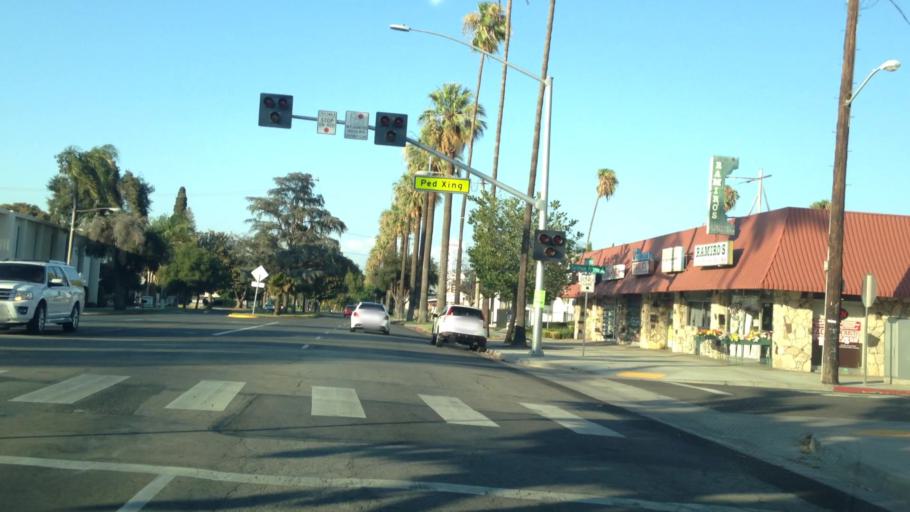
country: US
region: California
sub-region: Riverside County
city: Riverside
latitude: 33.9211
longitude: -117.4453
